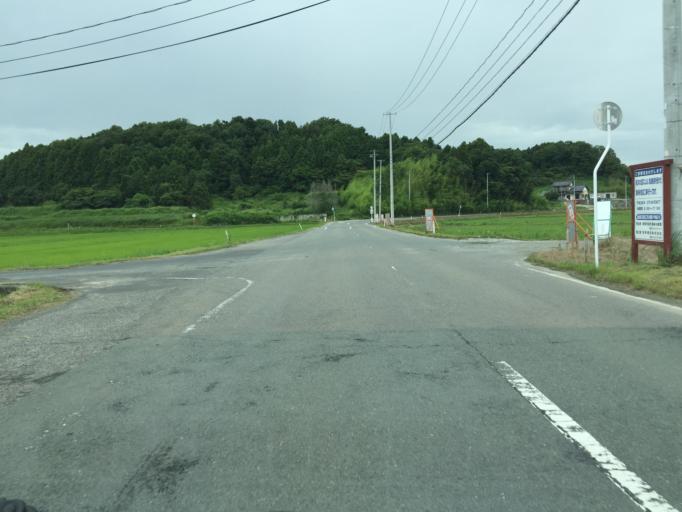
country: JP
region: Fukushima
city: Namie
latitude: 37.7534
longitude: 140.9978
